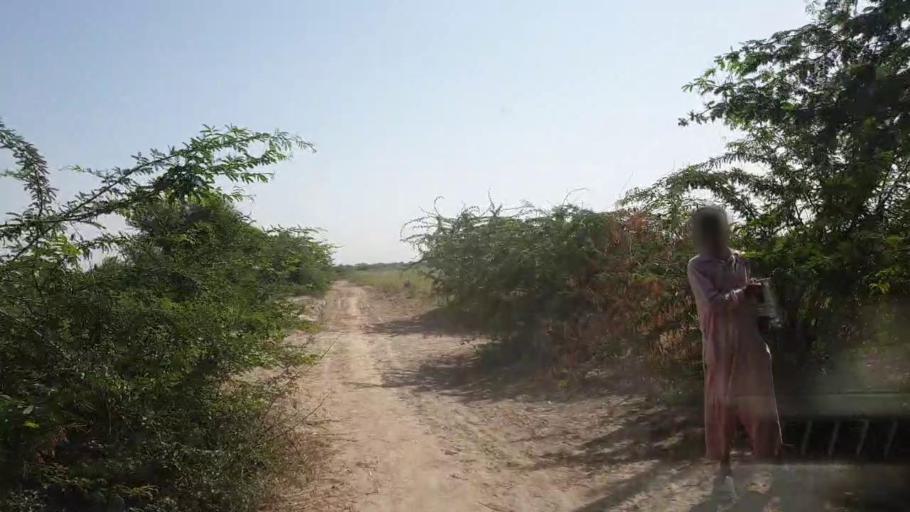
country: PK
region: Sindh
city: Kadhan
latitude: 24.5924
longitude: 69.0073
